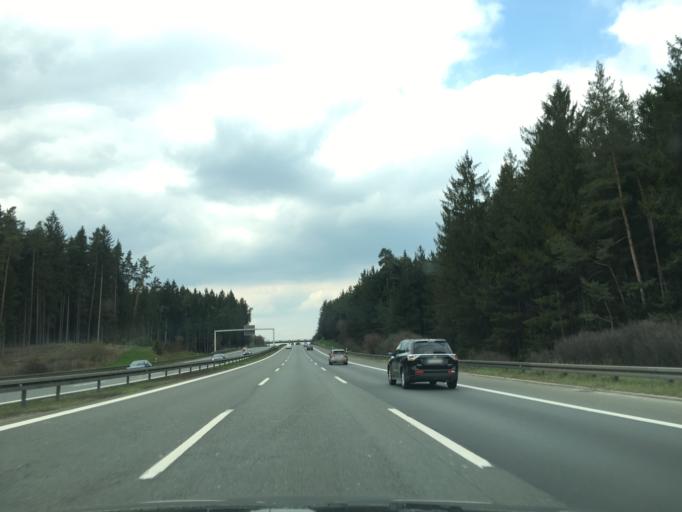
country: DE
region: Bavaria
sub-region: Regierungsbezirk Mittelfranken
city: Velden
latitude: 49.6759
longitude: 11.4683
